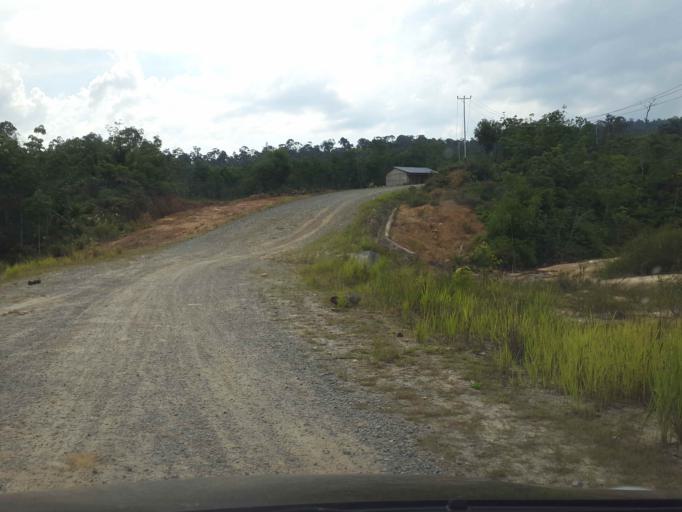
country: MY
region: Sarawak
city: Kuching
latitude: 1.7093
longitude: 109.5814
